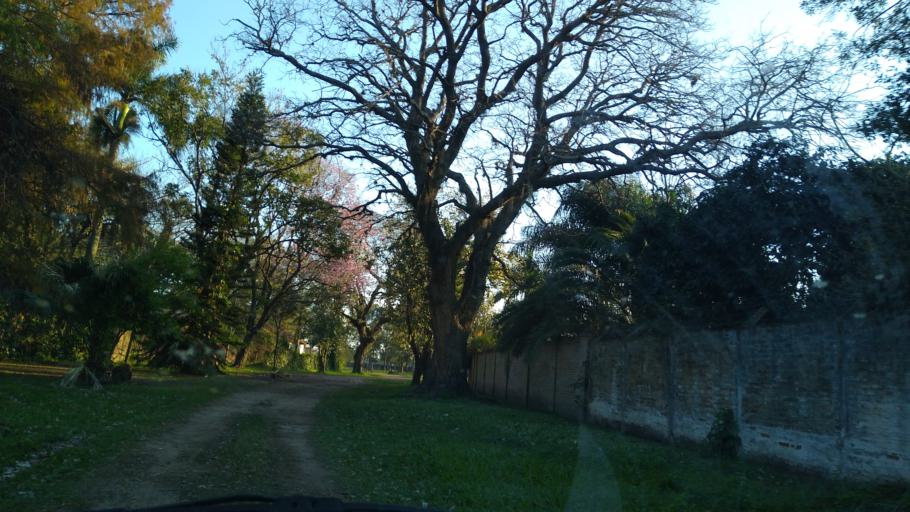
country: AR
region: Chaco
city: Barranqueras
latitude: -27.4672
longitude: -58.9554
